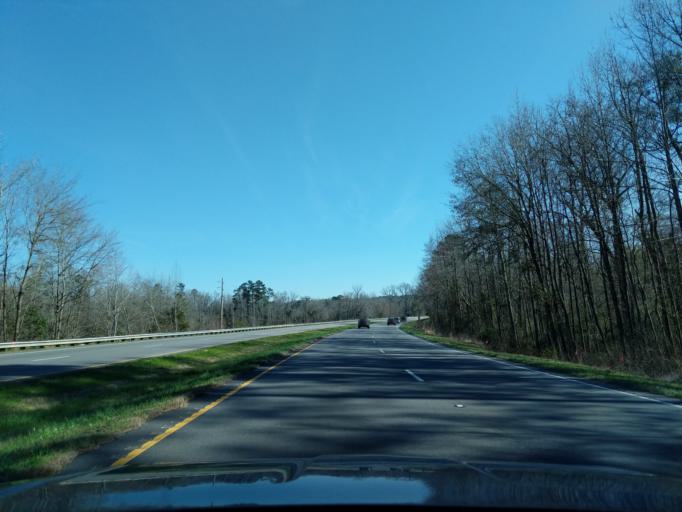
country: US
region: South Carolina
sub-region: Aiken County
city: Warrenville
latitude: 33.5521
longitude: -81.8182
